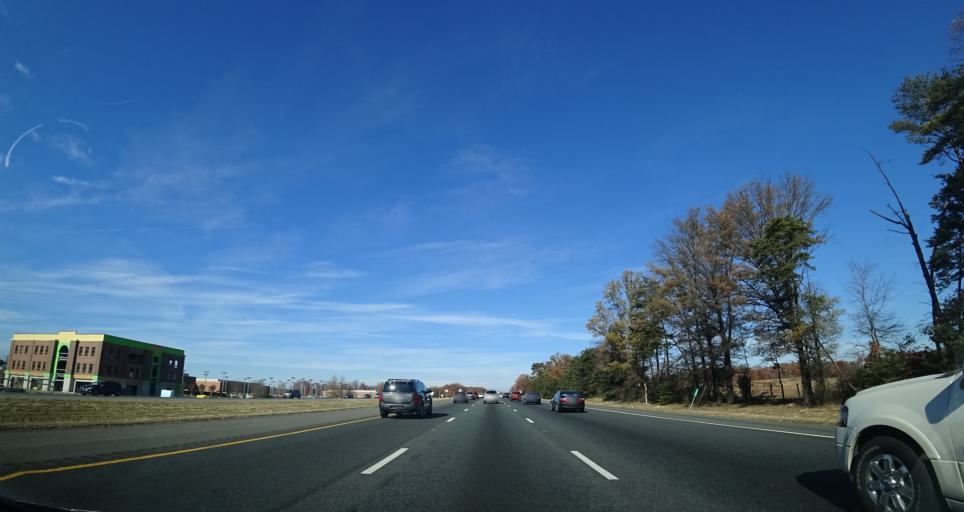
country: US
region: Virginia
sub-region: City of Fredericksburg
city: Fredericksburg
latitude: 38.2447
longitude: -77.5037
